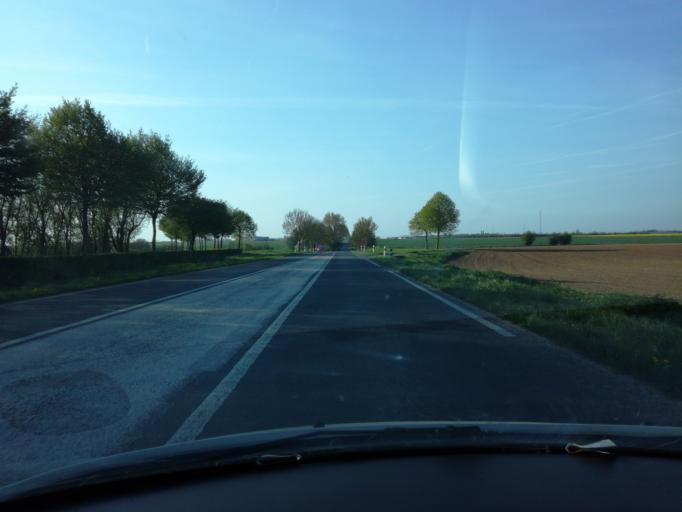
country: FR
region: Picardie
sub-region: Departement de la Somme
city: Poix-de-Picardie
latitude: 49.7993
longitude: 1.9733
